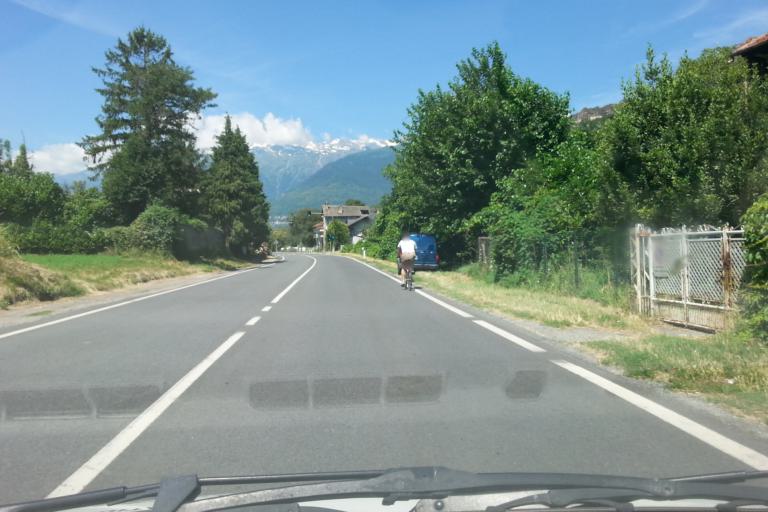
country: IT
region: Piedmont
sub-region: Provincia di Torino
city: Meana di Susa
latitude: 45.1387
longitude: 7.0854
